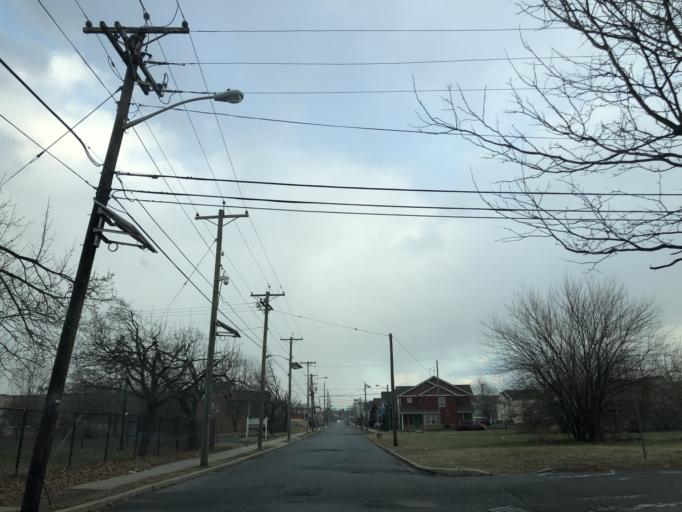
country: US
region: New Jersey
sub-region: Camden County
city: Camden
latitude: 39.9234
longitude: -75.1144
